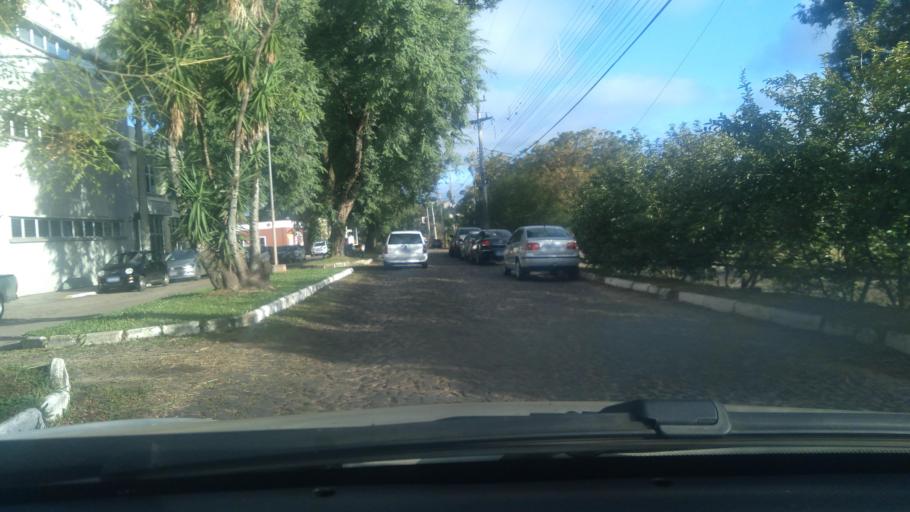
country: BR
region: Rio Grande do Sul
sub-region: Rosario Do Sul
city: Rosario do Sul
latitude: -30.2611
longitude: -54.9203
